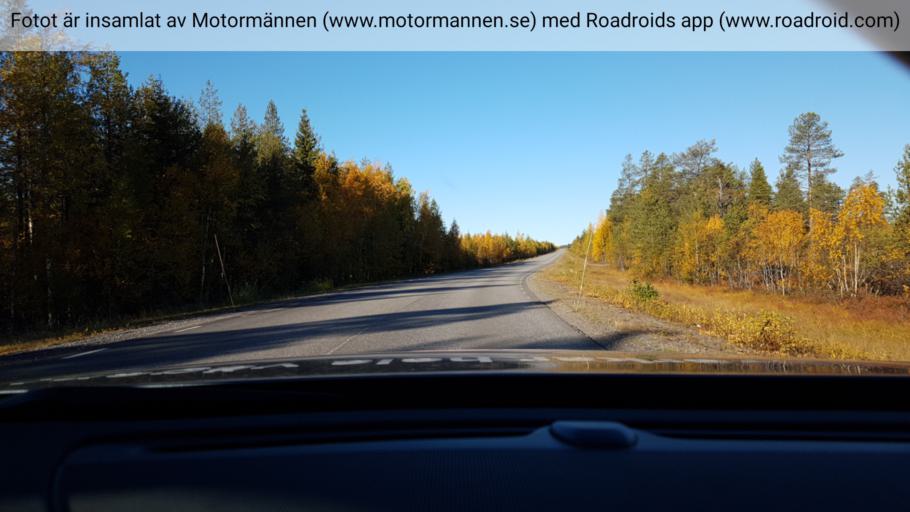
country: SE
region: Vaesterbotten
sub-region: Skelleftea Kommun
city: Storvik
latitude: 65.3249
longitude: 20.6987
